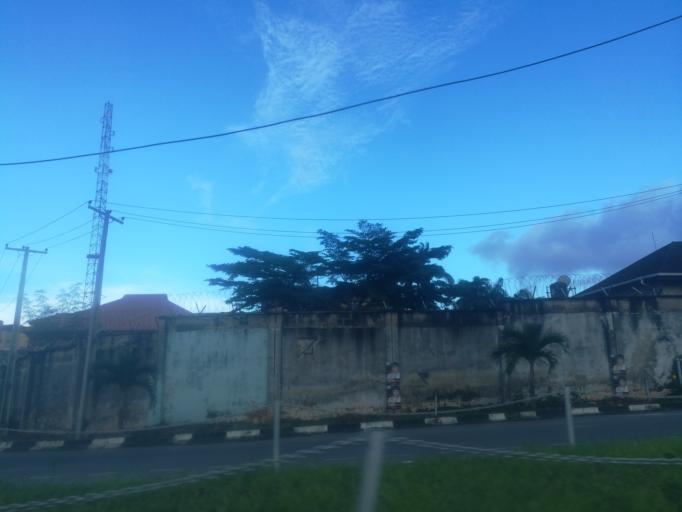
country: NG
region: Lagos
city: Ikeja
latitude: 6.6242
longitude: 3.3600
